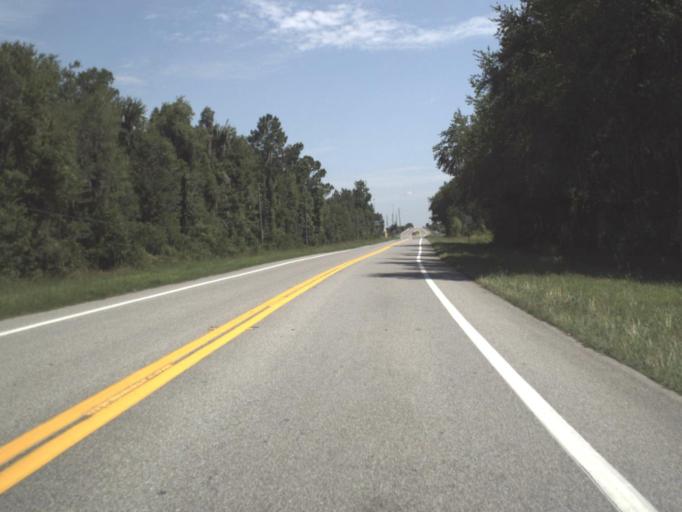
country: US
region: Florida
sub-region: Hamilton County
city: Jasper
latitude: 30.4413
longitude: -82.9338
